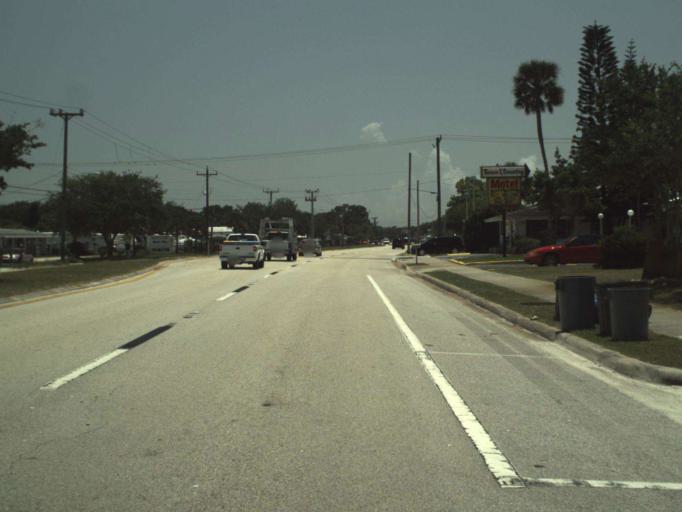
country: US
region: Florida
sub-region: Volusia County
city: Port Orange
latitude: 29.1223
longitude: -80.9770
